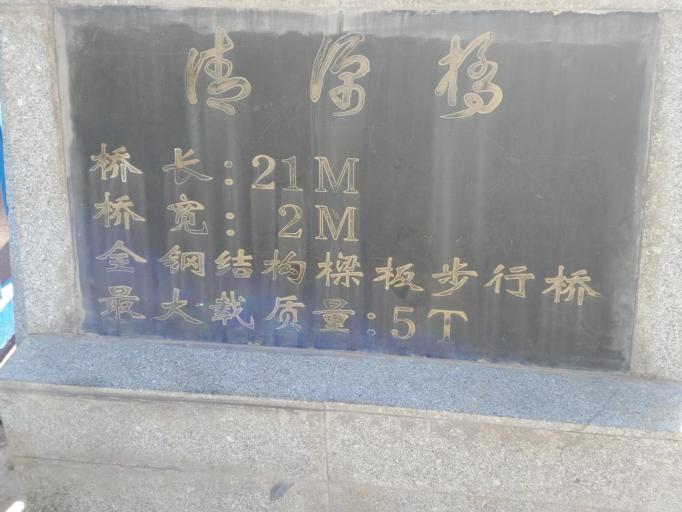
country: CN
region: Yunnan
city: Kunming
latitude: 25.0367
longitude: 102.6828
